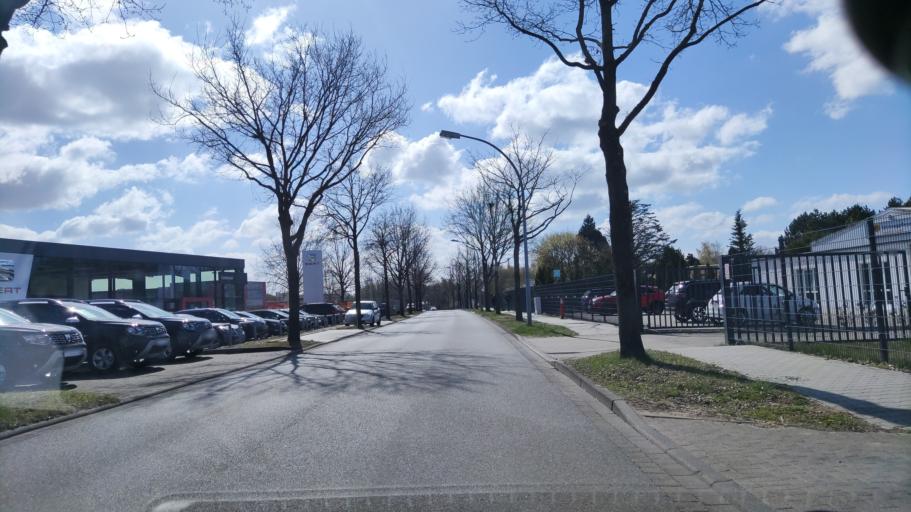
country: DE
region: Lower Saxony
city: Uelzen
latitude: 52.9927
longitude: 10.5398
